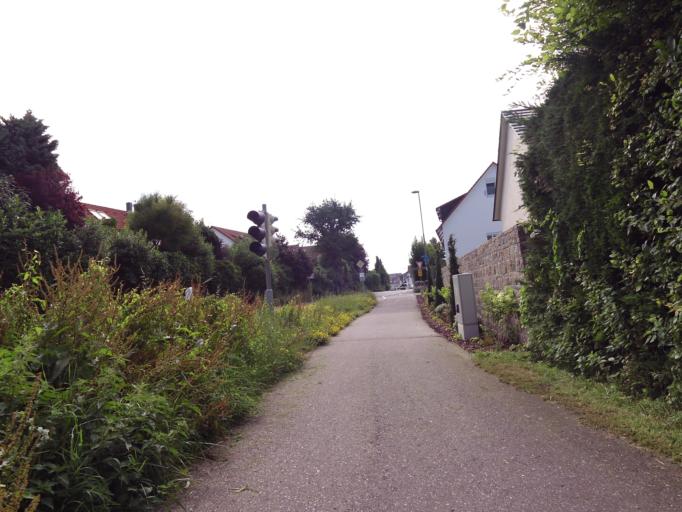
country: DE
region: Baden-Wuerttemberg
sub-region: Freiburg Region
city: Allensbach
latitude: 47.7216
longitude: 9.0506
